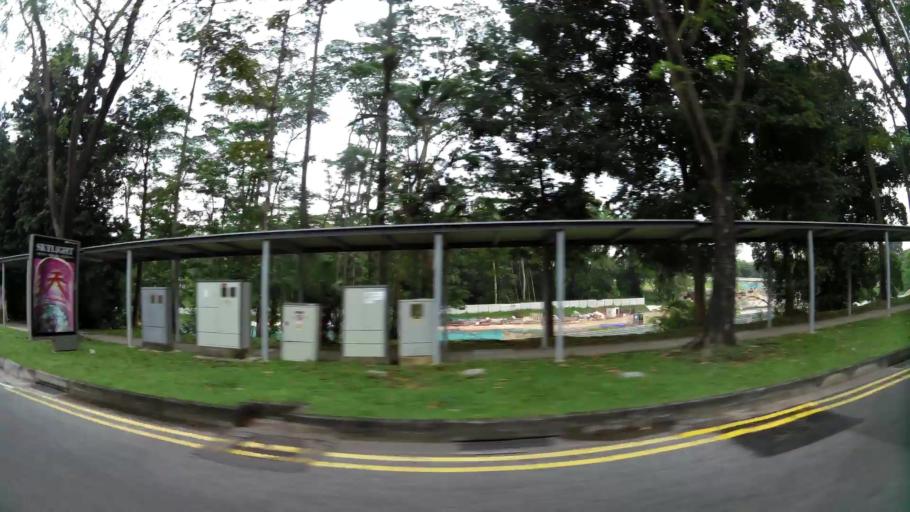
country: SG
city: Singapore
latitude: 1.3416
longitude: 103.8709
